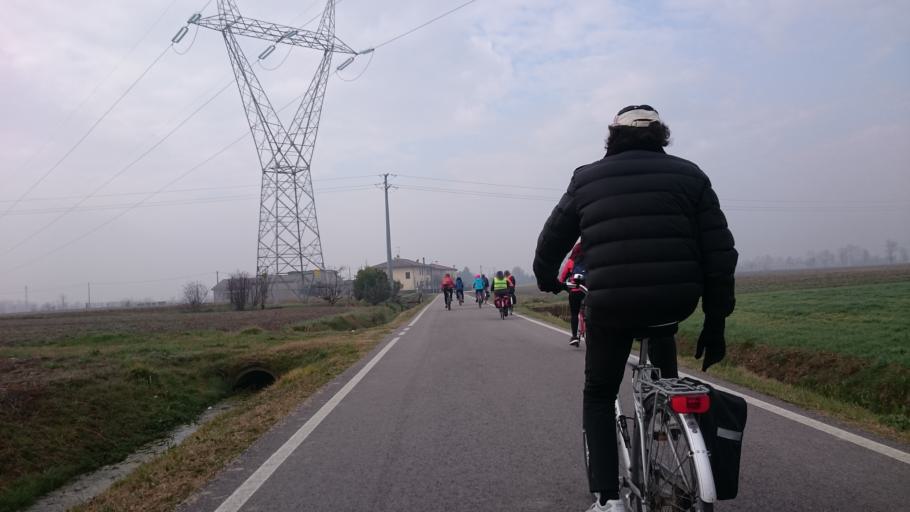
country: IT
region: Veneto
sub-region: Provincia di Vicenza
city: Longare
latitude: 45.4790
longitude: 11.6477
